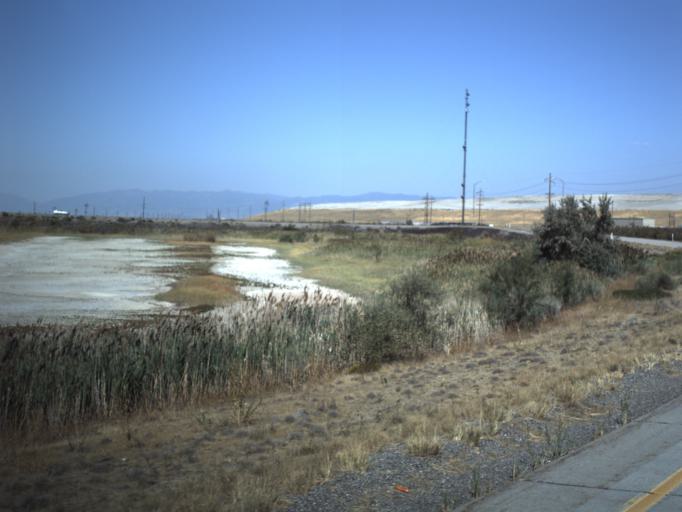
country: US
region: Utah
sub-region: Salt Lake County
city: Magna
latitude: 40.7420
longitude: -112.1831
